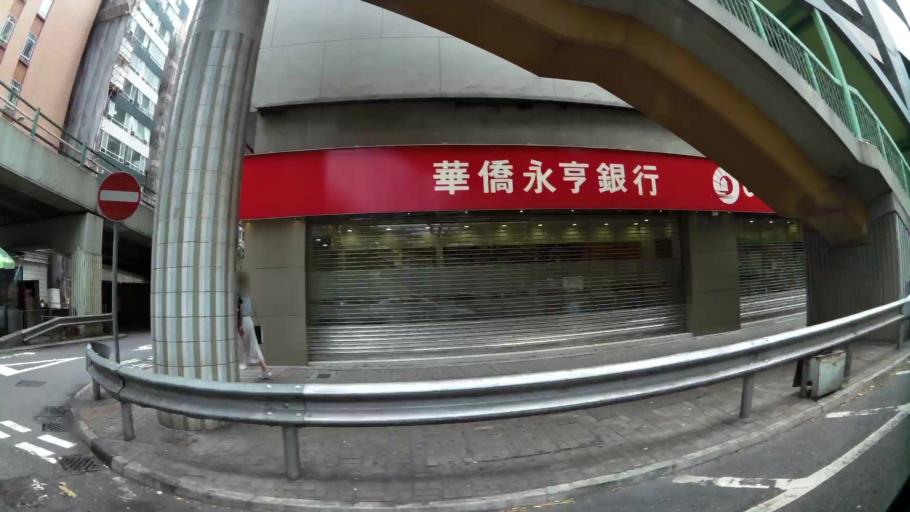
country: HK
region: Wanchai
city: Wan Chai
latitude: 22.2794
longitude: 114.1744
